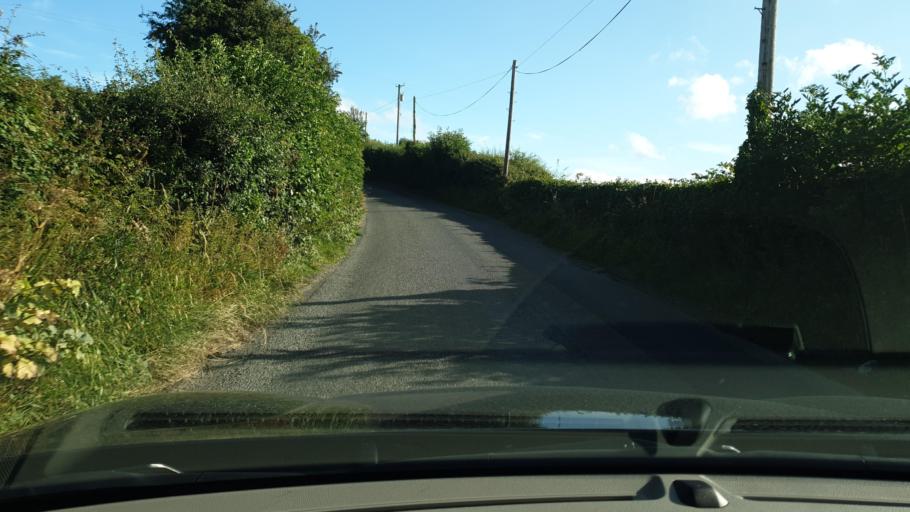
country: IE
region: Leinster
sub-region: An Mhi
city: Stamullin
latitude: 53.6153
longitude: -6.2938
